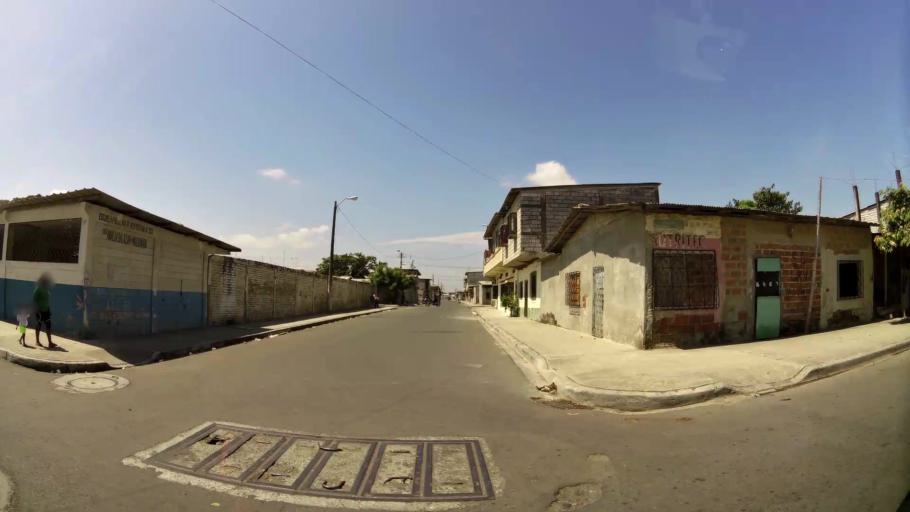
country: EC
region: Guayas
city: Guayaquil
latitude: -2.2325
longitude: -79.9194
